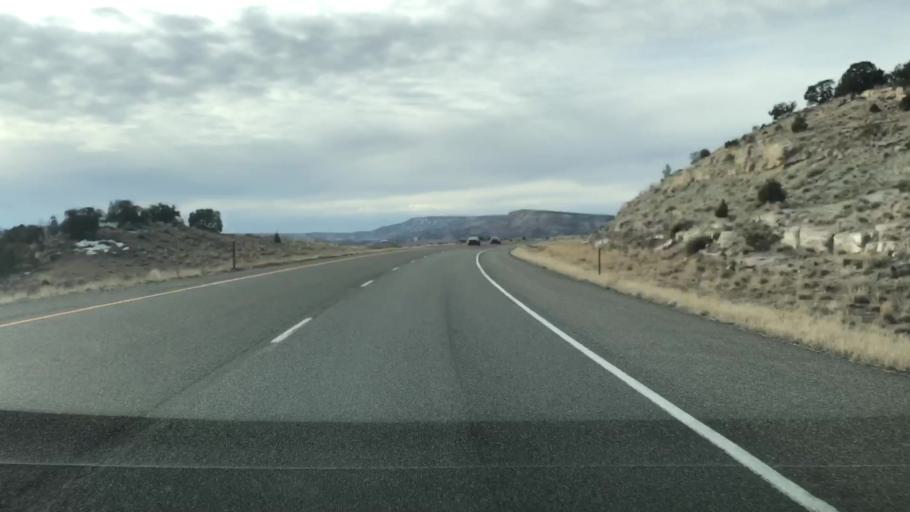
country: US
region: Colorado
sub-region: Mesa County
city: Loma
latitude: 39.2122
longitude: -108.9678
